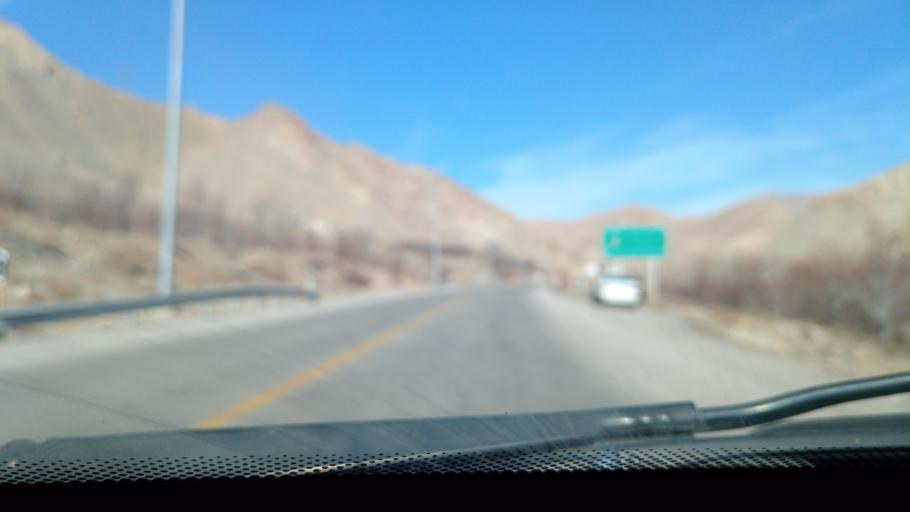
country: IR
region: Khorasan-e Shomali
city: Esfarayen
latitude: 37.1834
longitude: 57.4134
